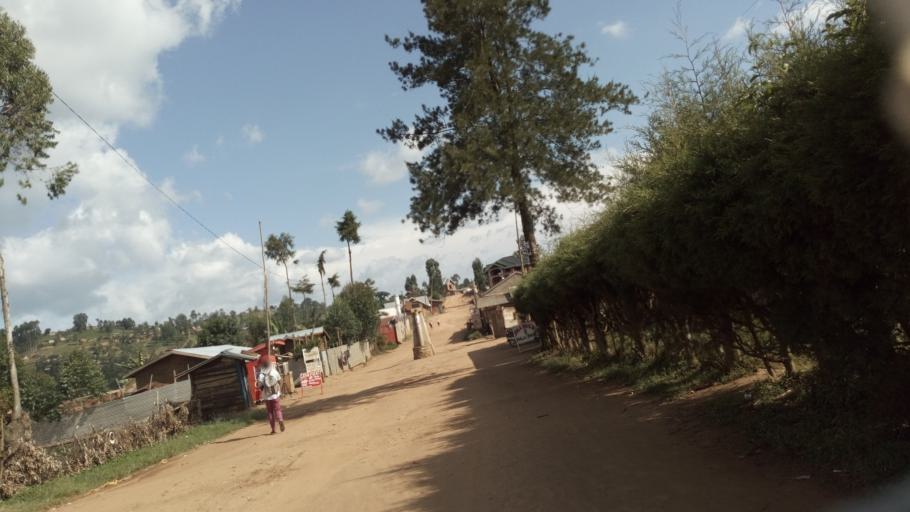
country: CD
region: Nord Kivu
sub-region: North Kivu
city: Butembo
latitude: 0.1112
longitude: 29.3227
